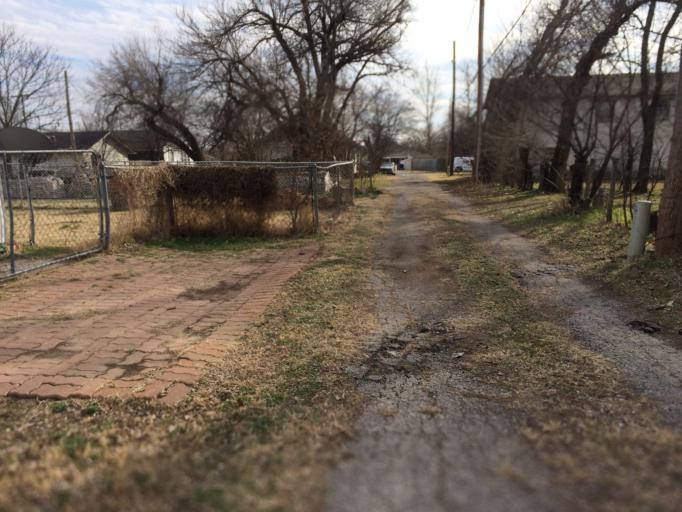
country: US
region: Oklahoma
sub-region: Cleveland County
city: Norman
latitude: 35.2265
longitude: -97.4334
